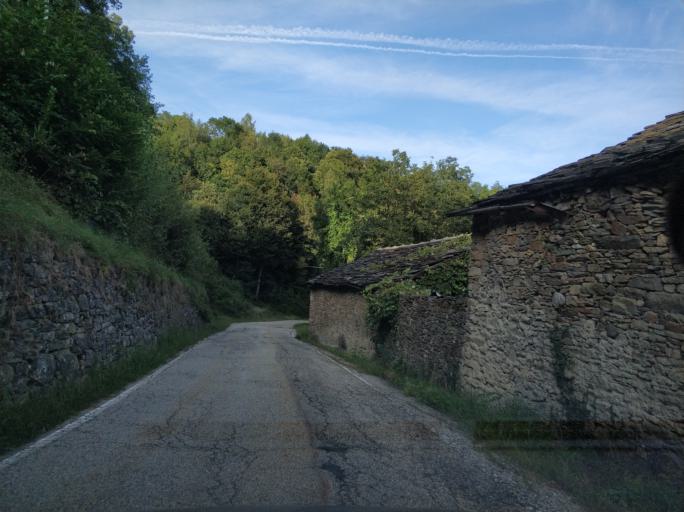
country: IT
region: Piedmont
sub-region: Provincia di Torino
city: Monastero di Lanzo
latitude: 45.3036
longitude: 7.4414
